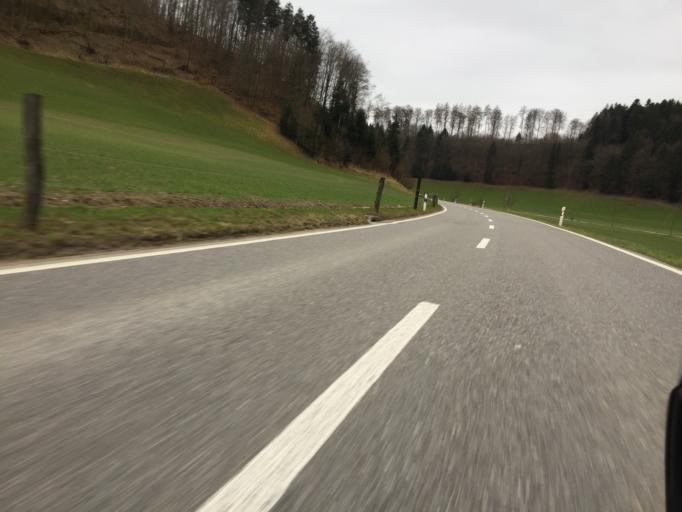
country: CH
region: Bern
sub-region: Emmental District
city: Krauchthal
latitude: 47.0205
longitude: 7.5723
